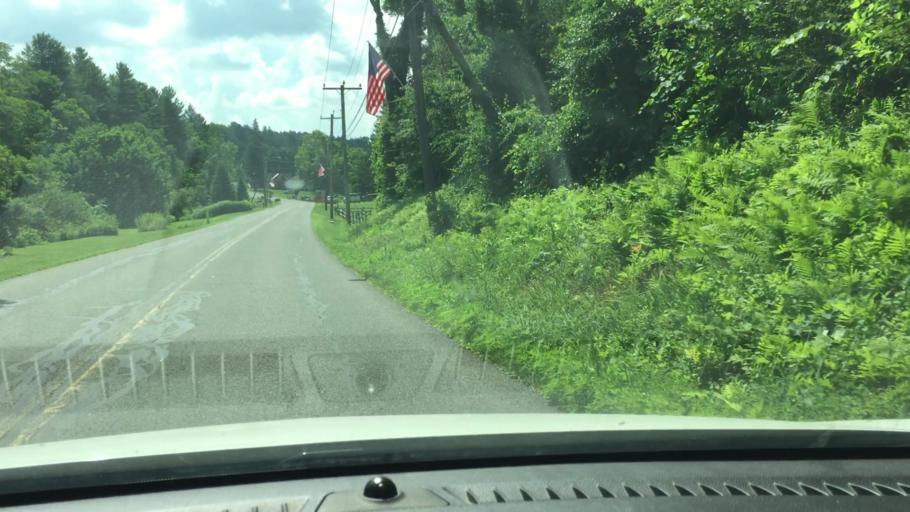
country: US
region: Massachusetts
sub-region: Berkshire County
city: Lee
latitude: 42.2433
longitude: -73.2005
